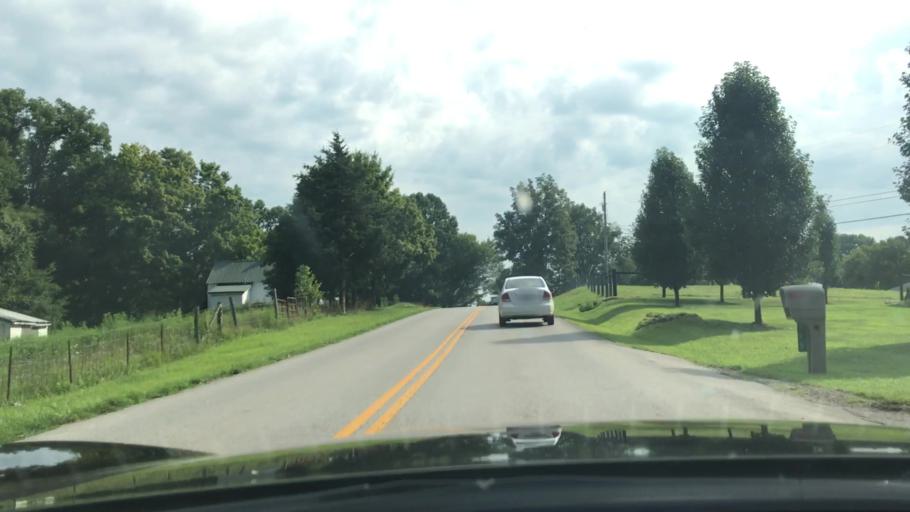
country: US
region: Kentucky
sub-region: Green County
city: Greensburg
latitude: 37.2761
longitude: -85.5241
